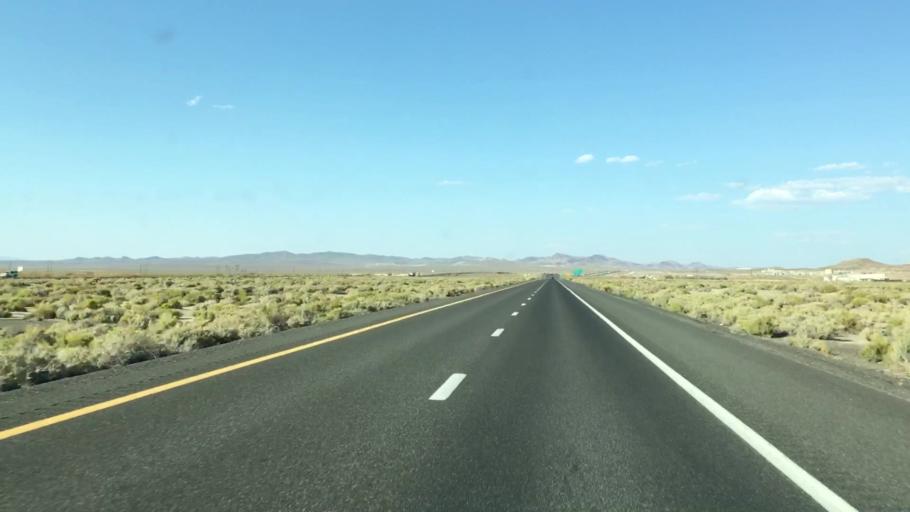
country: US
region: Nevada
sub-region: Lyon County
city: Fernley
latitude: 39.7826
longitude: -119.0267
